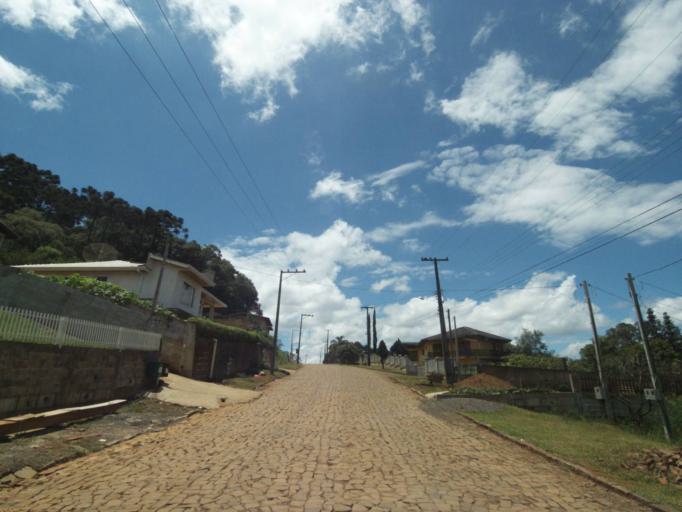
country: BR
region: Parana
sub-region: Uniao Da Vitoria
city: Uniao da Vitoria
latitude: -26.1625
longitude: -51.5564
